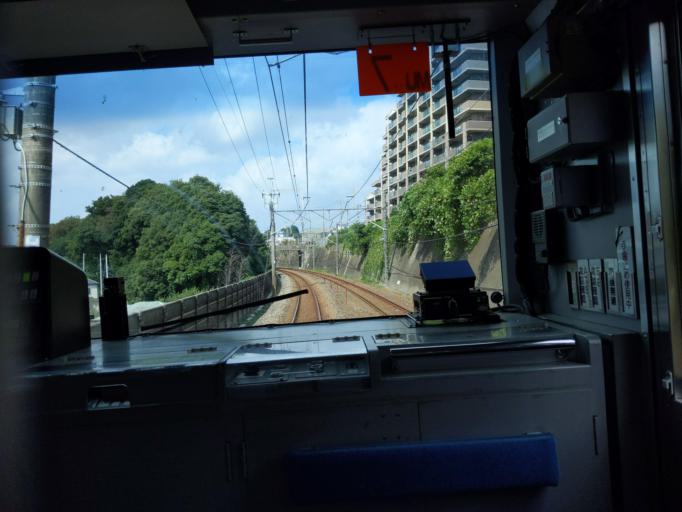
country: JP
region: Chiba
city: Nagareyama
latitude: 35.8211
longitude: 139.9278
